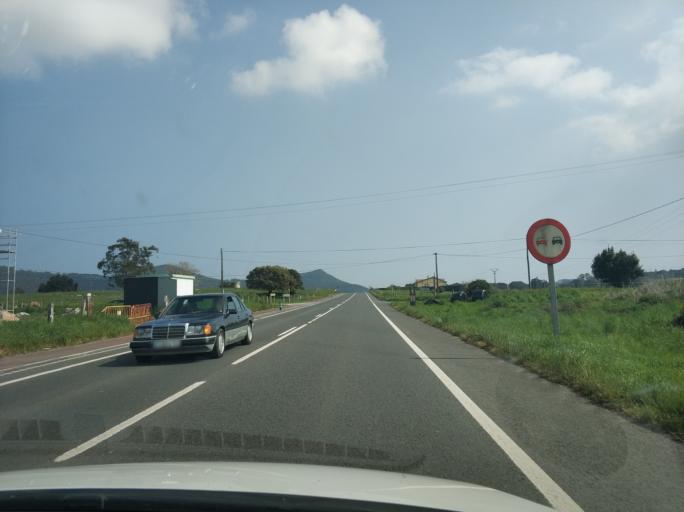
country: ES
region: Cantabria
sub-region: Provincia de Cantabria
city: Escalante
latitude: 43.4446
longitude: -3.5021
